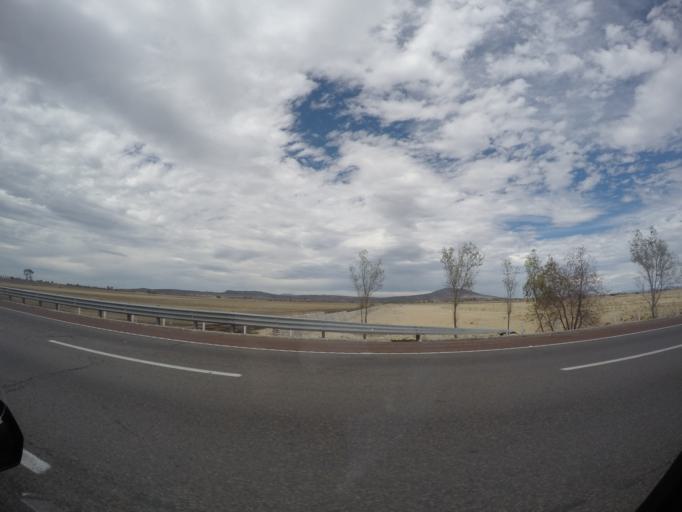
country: MX
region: Queretaro
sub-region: San Juan del Rio
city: El Cazadero
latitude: 20.2755
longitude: -99.8878
